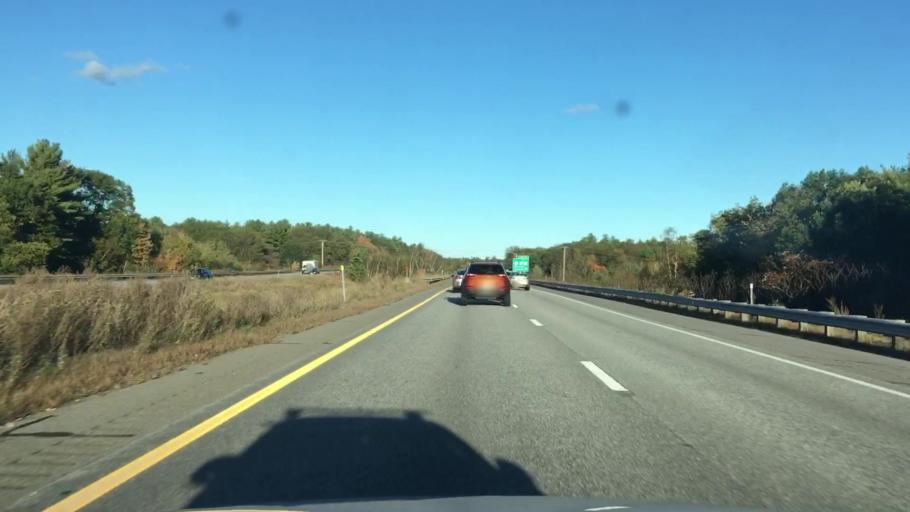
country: US
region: New Hampshire
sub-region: Rockingham County
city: Raymond
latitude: 43.0290
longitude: -71.1687
